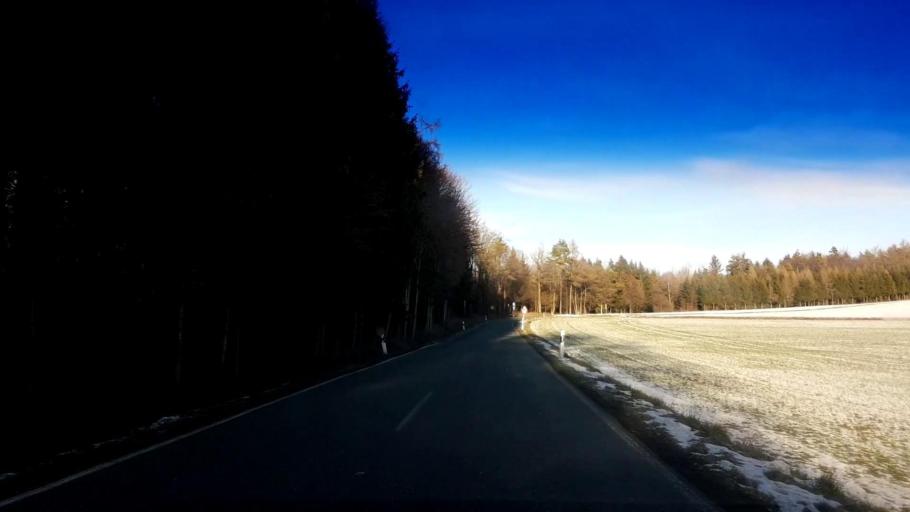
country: DE
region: Bavaria
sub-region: Upper Franconia
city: Heiligenstadt
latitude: 49.8554
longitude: 11.1497
